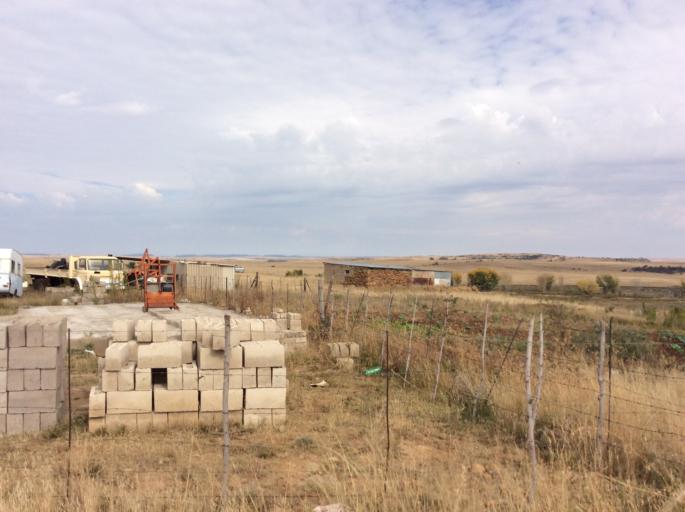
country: LS
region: Mafeteng
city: Mafeteng
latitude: -29.7221
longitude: 27.0067
